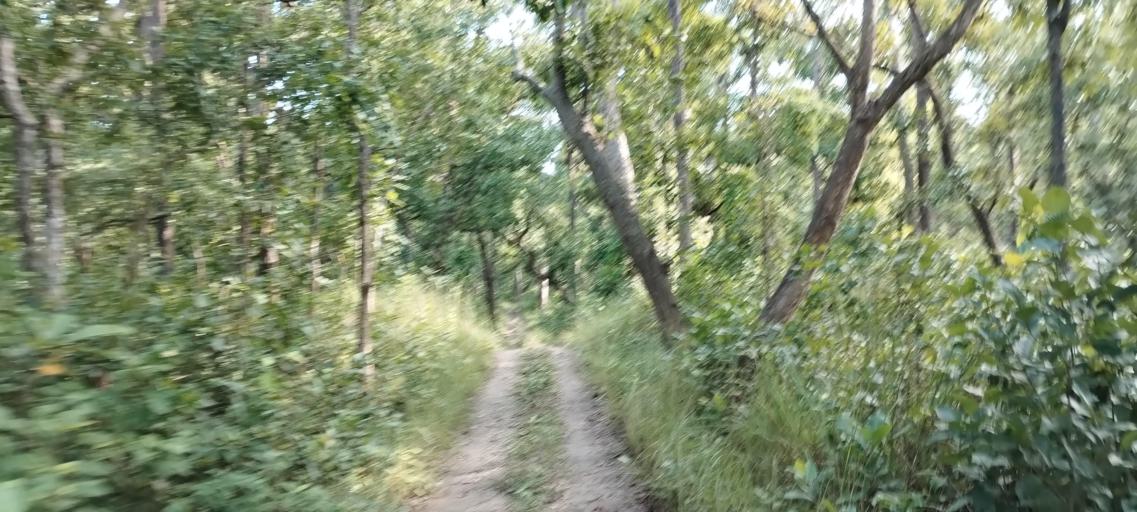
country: NP
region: Far Western
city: Tikapur
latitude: 28.5458
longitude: 81.2865
